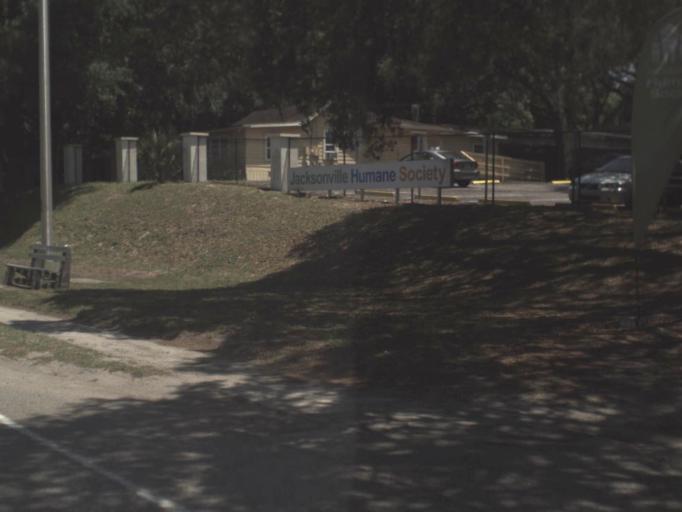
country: US
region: Florida
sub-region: Duval County
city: Jacksonville
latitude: 30.2876
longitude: -81.5716
